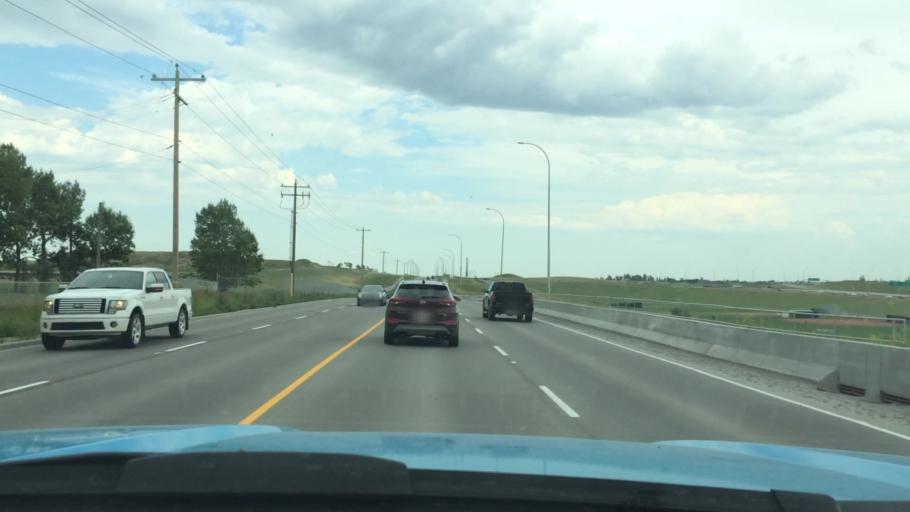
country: CA
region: Alberta
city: Calgary
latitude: 51.1541
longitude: -114.1833
